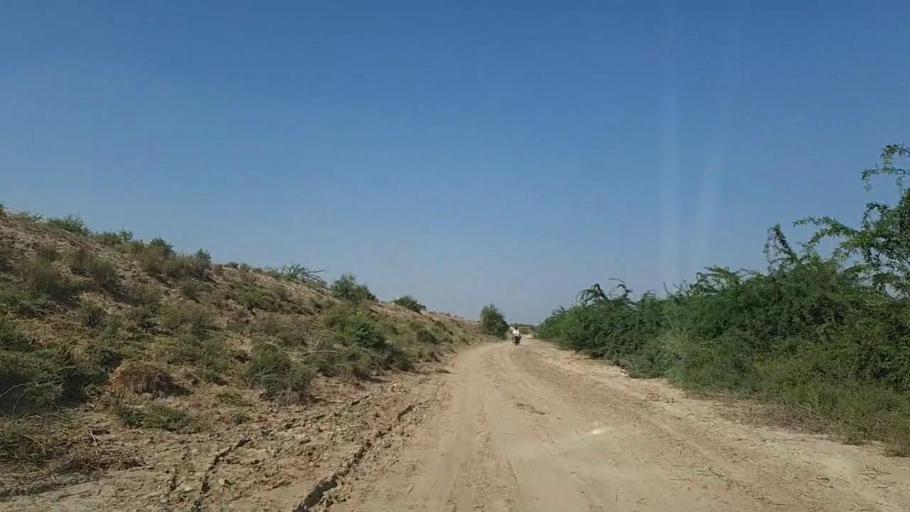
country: PK
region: Sindh
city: Chuhar Jamali
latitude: 24.5763
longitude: 68.0296
